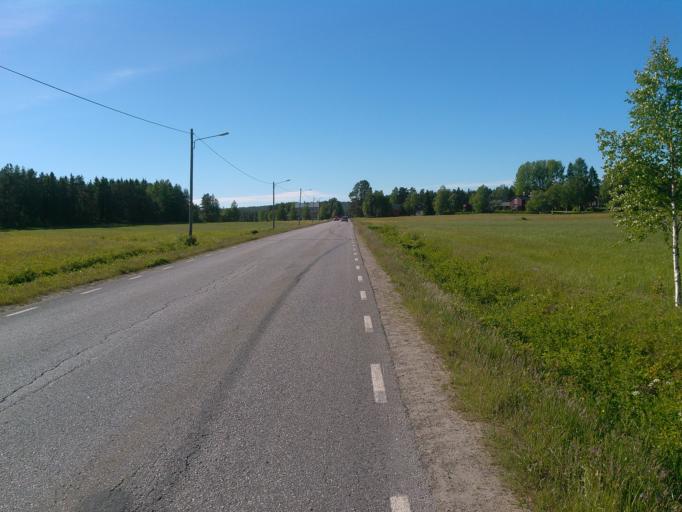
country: SE
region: Vaesterbotten
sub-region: Umea Kommun
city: Roback
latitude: 63.8271
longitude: 20.1191
